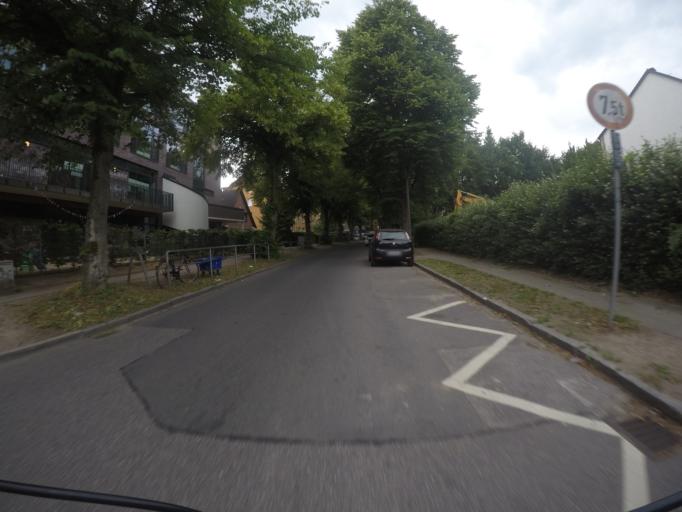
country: DE
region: Hamburg
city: Eidelstedt
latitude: 53.6030
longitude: 9.9038
